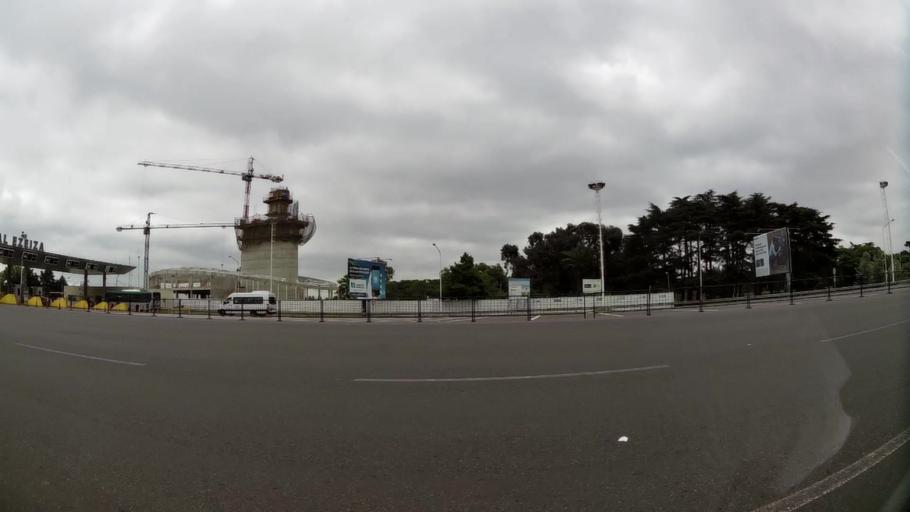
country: AR
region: Buenos Aires
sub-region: Partido de Ezeiza
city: Ezeiza
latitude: -34.8091
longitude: -58.5433
